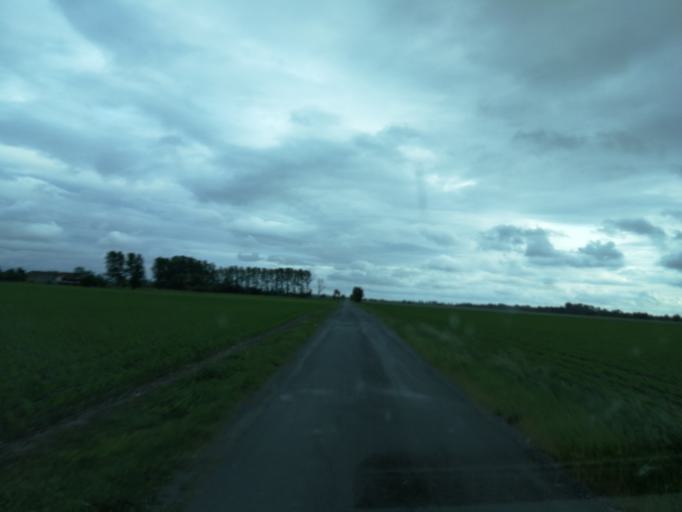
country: FR
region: Pays de la Loire
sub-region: Departement de la Vendee
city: Le Langon
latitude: 46.3699
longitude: -0.9318
